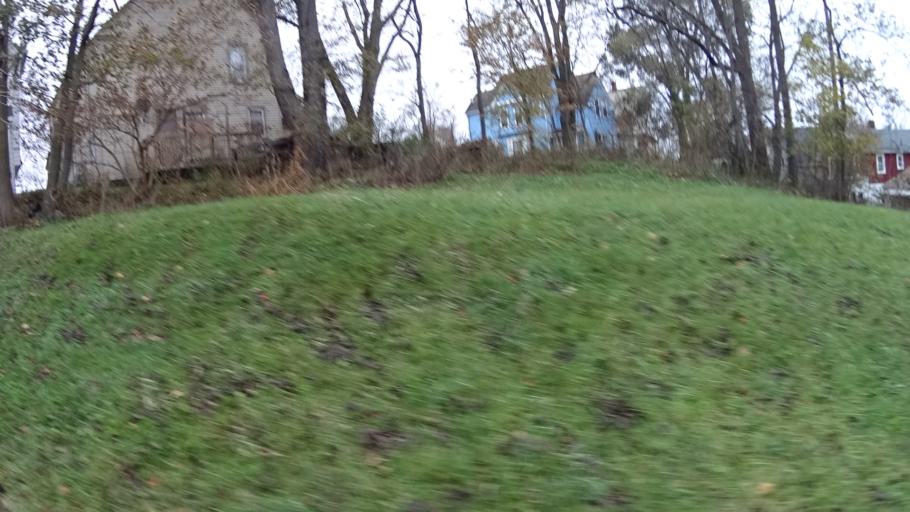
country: US
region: Ohio
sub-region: Lorain County
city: Elyria
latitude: 41.3682
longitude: -82.1148
